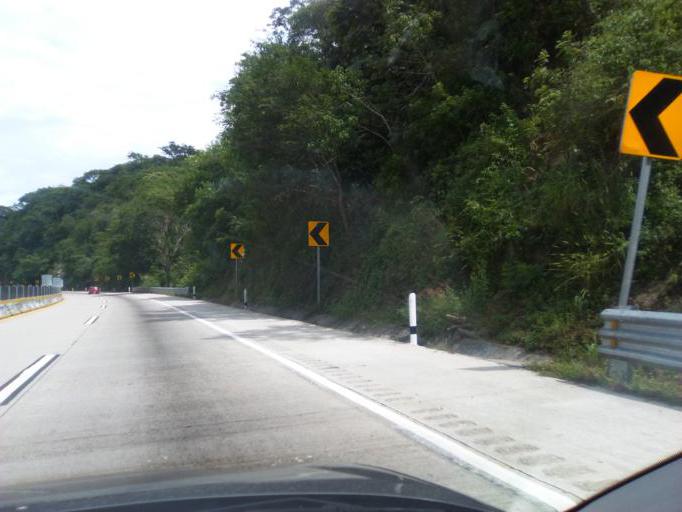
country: MX
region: Guerrero
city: Tierra Colorada
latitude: 17.1908
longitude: -99.5352
